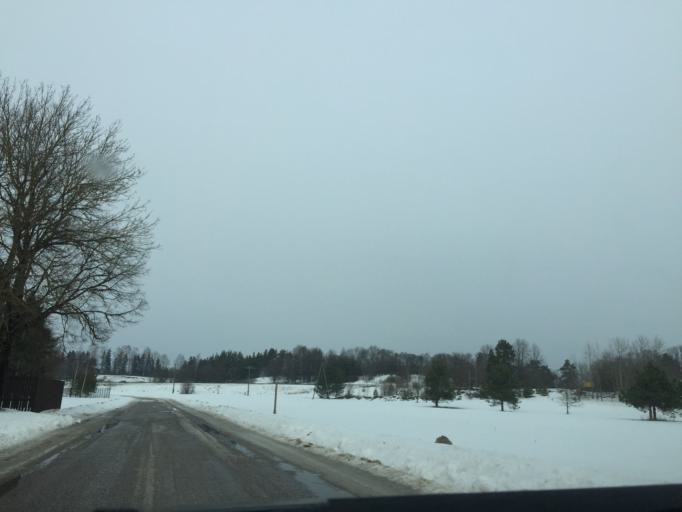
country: LV
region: Ikskile
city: Ikskile
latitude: 56.8426
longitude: 24.4721
